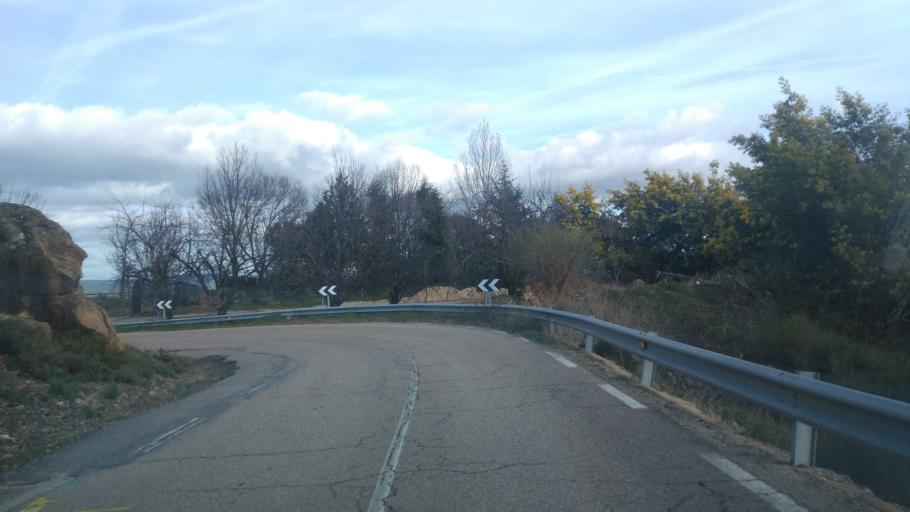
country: ES
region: Castille and Leon
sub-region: Provincia de Salamanca
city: Mogarraz
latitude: 40.4927
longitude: -6.0409
